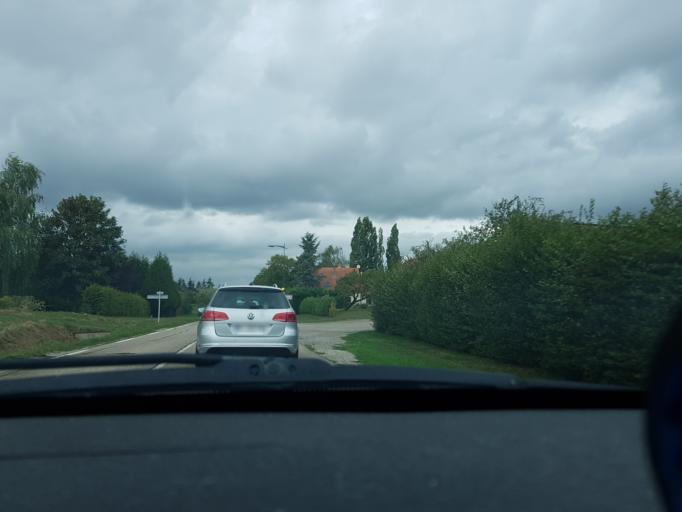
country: FR
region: Lorraine
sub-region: Departement de la Moselle
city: Morhange
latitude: 48.9796
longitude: 6.6050
